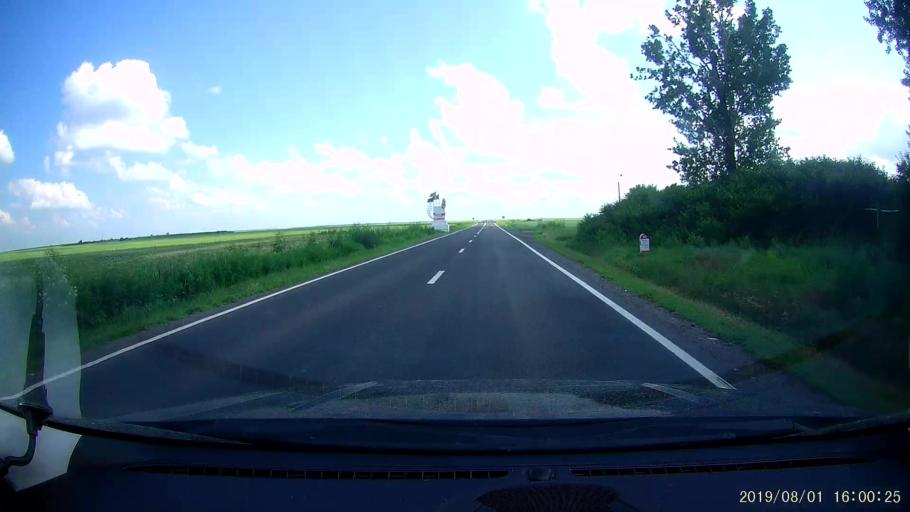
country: RO
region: Ialomita
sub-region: Comuna Ciulnita
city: Ciulnita
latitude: 44.5301
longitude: 27.3887
